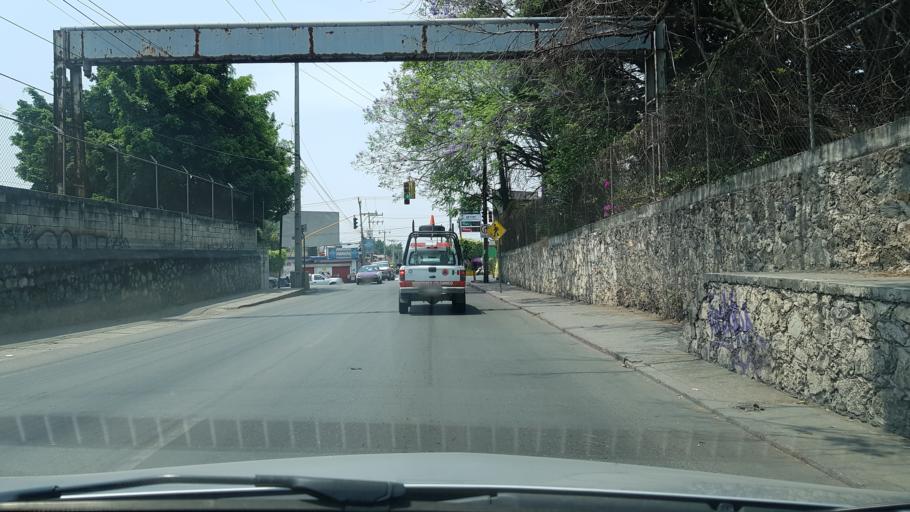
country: MX
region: Morelos
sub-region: Jiutepec
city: Jiutepec
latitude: 18.8910
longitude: -99.1727
